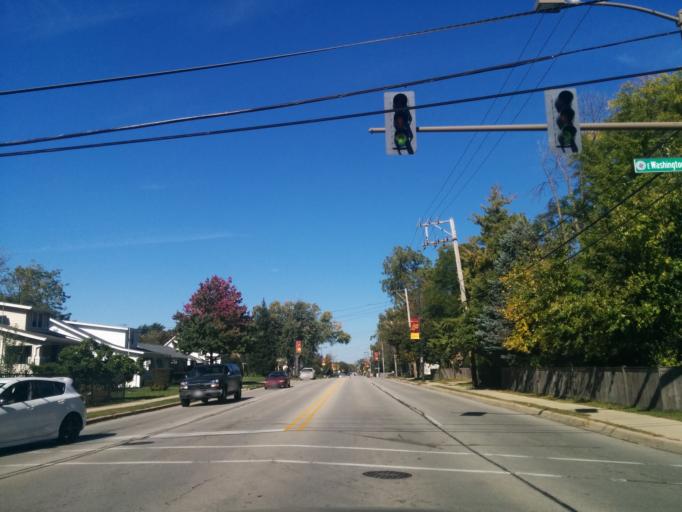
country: US
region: Illinois
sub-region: DuPage County
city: Villa Park
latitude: 41.8784
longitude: -87.9936
